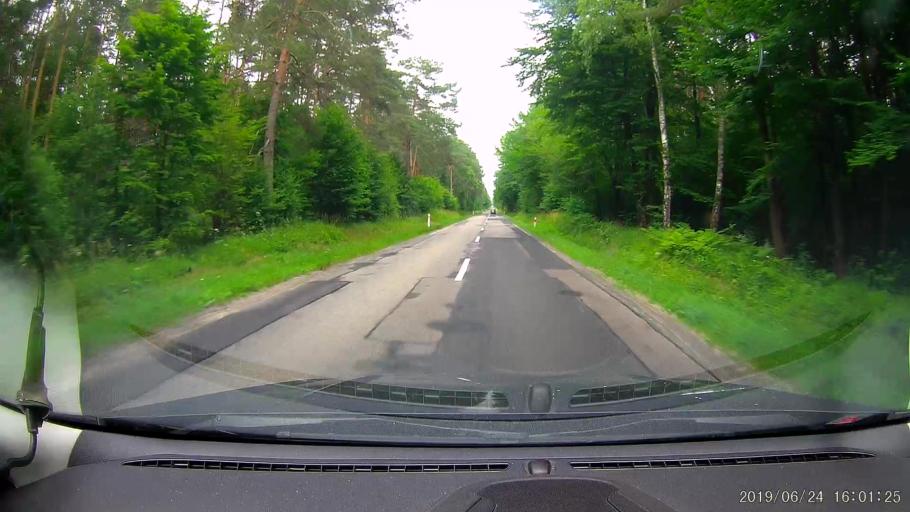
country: PL
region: Subcarpathian Voivodeship
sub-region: Powiat lubaczowski
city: Nowe Siolo
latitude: 50.2921
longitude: 23.1966
